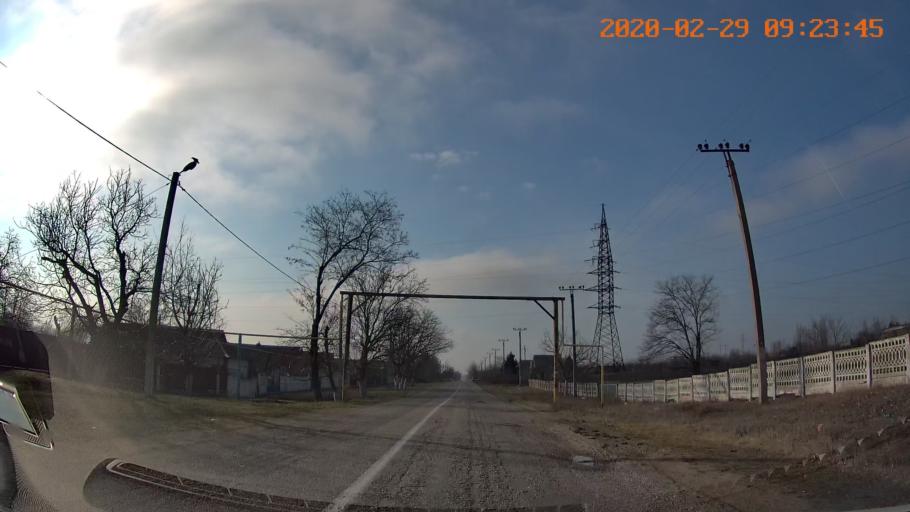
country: MD
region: Telenesti
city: Pervomaisc
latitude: 46.7228
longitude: 29.9604
